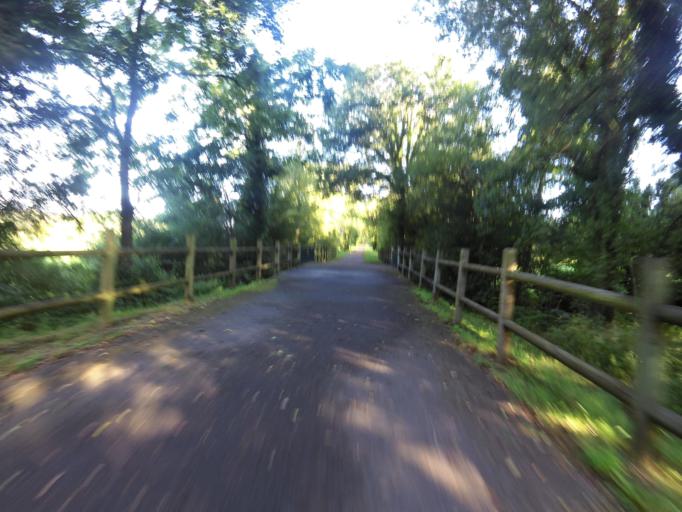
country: FR
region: Brittany
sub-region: Departement du Morbihan
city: Malestroit
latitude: 47.8377
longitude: -2.4279
